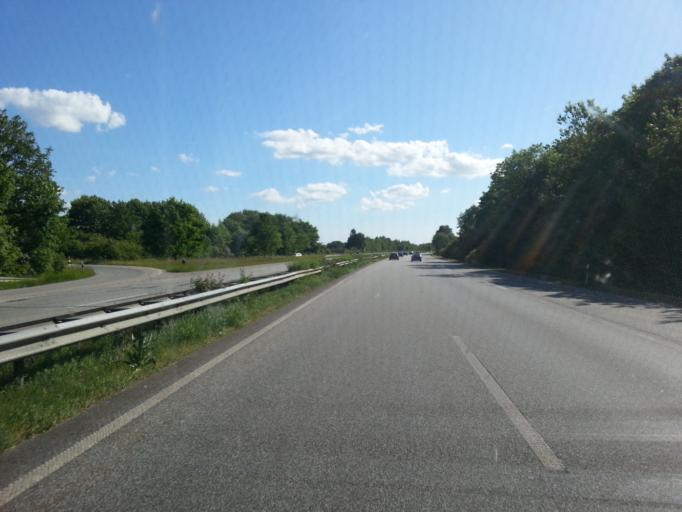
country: DE
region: Schleswig-Holstein
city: Sierksdorf
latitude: 54.0944
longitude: 10.7757
